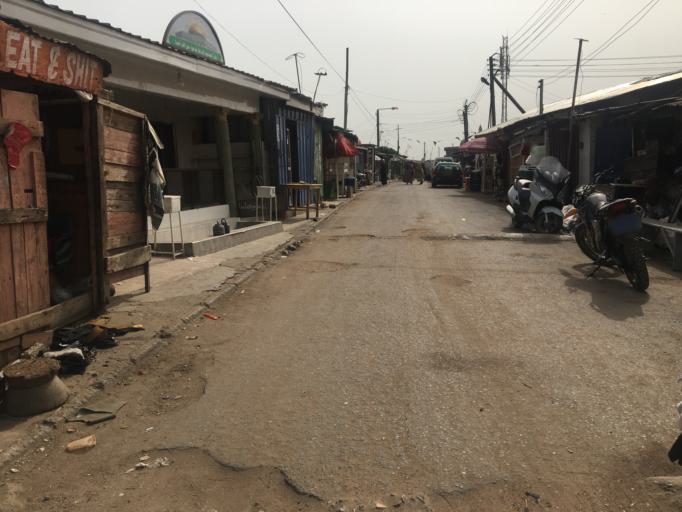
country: GH
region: Greater Accra
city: Accra
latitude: 5.5898
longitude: -0.1936
